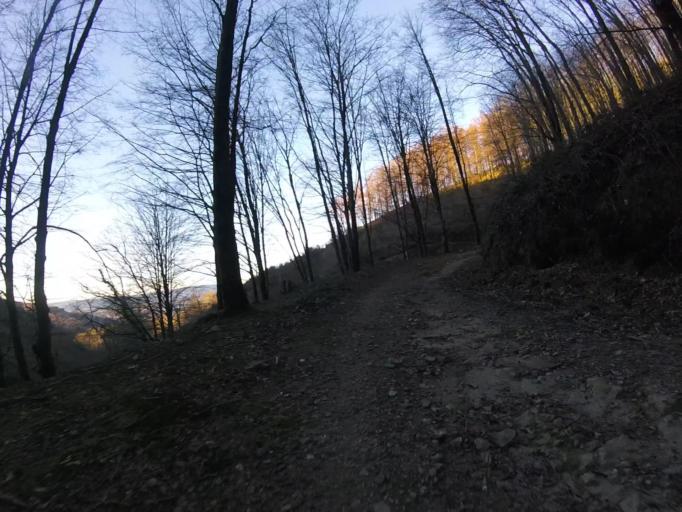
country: ES
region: Navarre
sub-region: Provincia de Navarra
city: Arano
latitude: 43.2582
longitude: -1.8356
